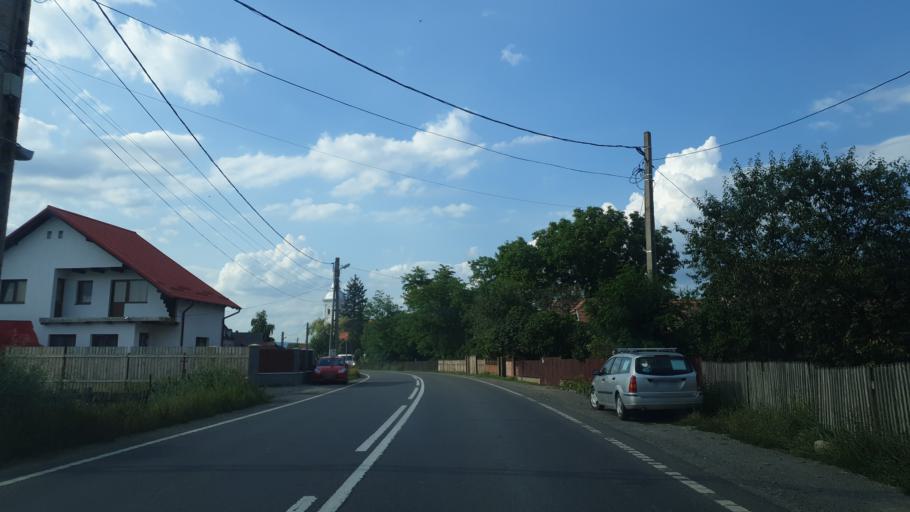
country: RO
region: Covasna
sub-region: Comuna Chichis
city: Chichis
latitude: 45.8111
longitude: 25.8003
